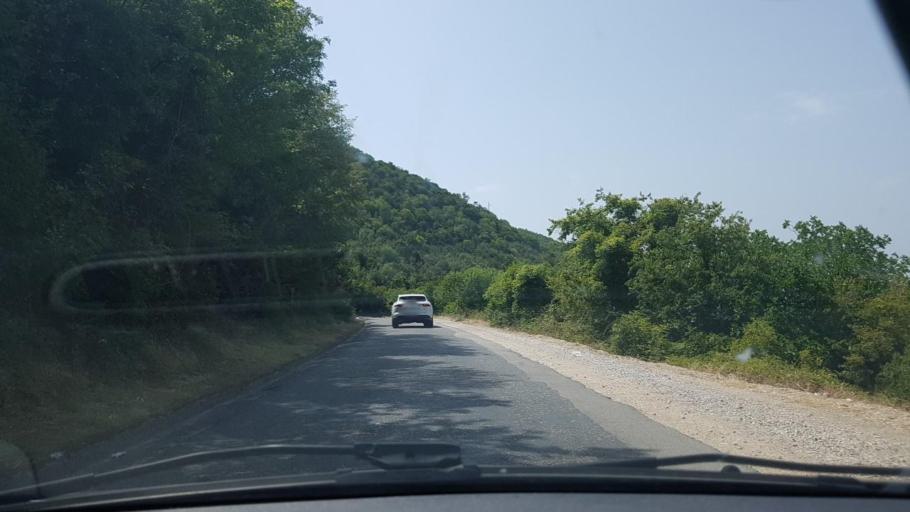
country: BA
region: Federation of Bosnia and Herzegovina
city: Tasovcici
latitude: 43.0284
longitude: 17.7478
